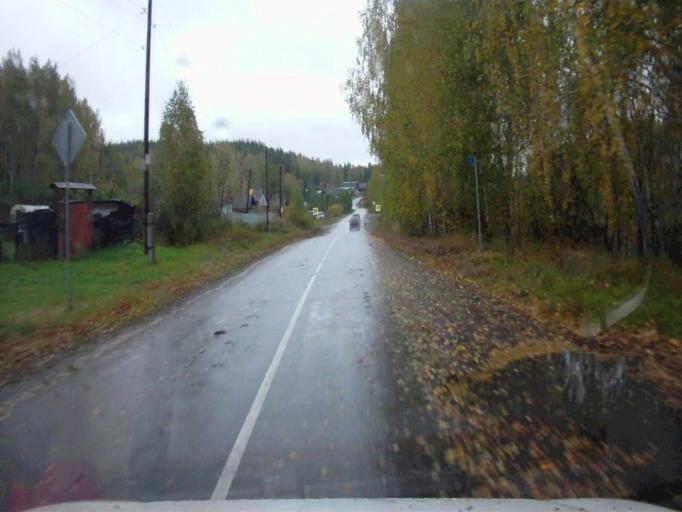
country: RU
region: Chelyabinsk
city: Kyshtym
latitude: 55.7620
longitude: 60.4860
